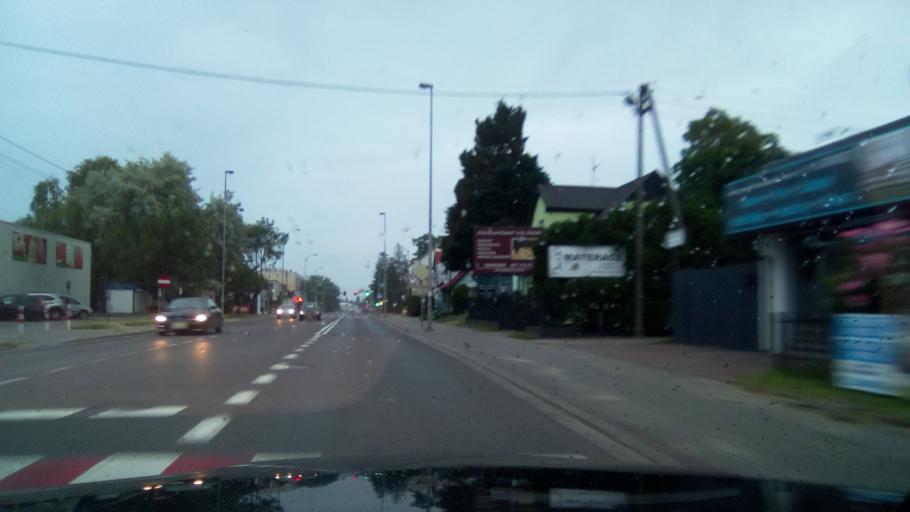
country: PL
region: Greater Poland Voivodeship
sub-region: Powiat poznanski
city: Swarzedz
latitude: 52.4107
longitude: 17.0847
